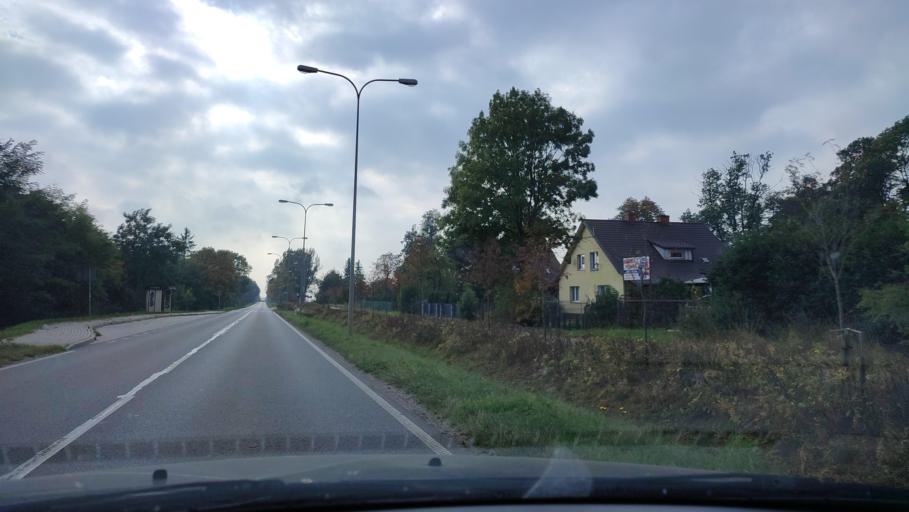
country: PL
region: Warmian-Masurian Voivodeship
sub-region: Powiat nidzicki
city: Nidzica
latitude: 53.3510
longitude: 20.3585
